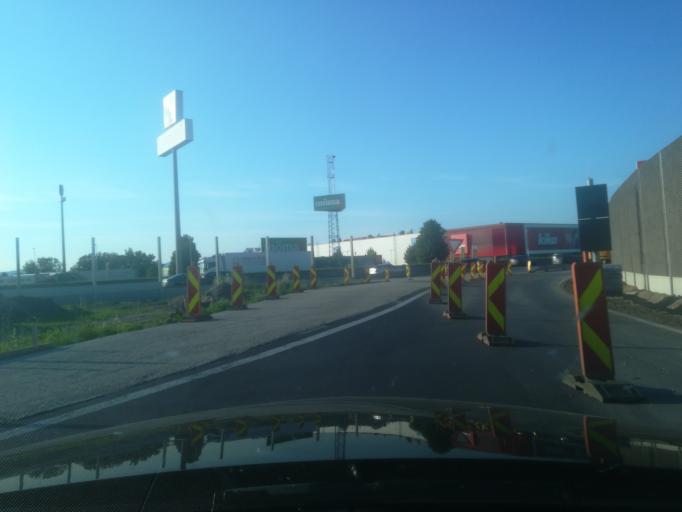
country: AT
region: Upper Austria
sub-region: Politischer Bezirk Linz-Land
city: Ansfelden
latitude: 48.2141
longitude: 14.2849
